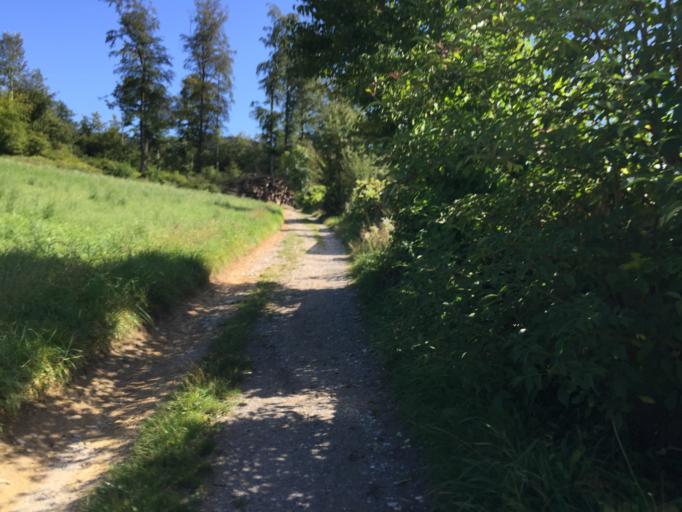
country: CH
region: Bern
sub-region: Bern-Mittelland District
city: Koniz
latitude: 46.9191
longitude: 7.4215
